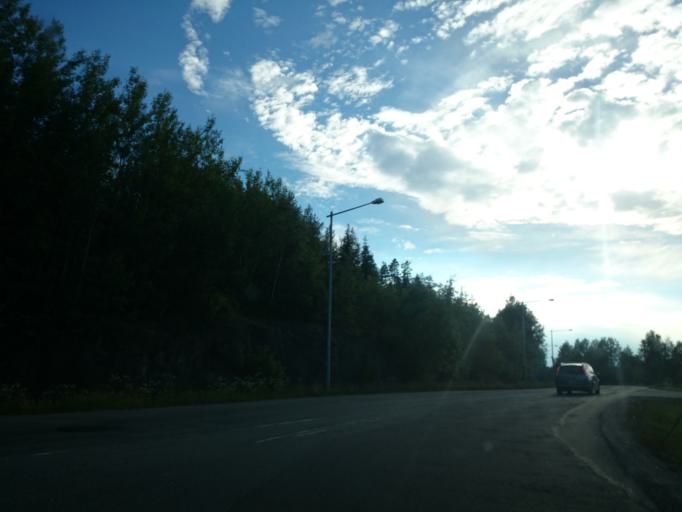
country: SE
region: Vaesternorrland
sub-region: Timra Kommun
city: Bergeforsen
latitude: 62.5156
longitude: 17.3911
